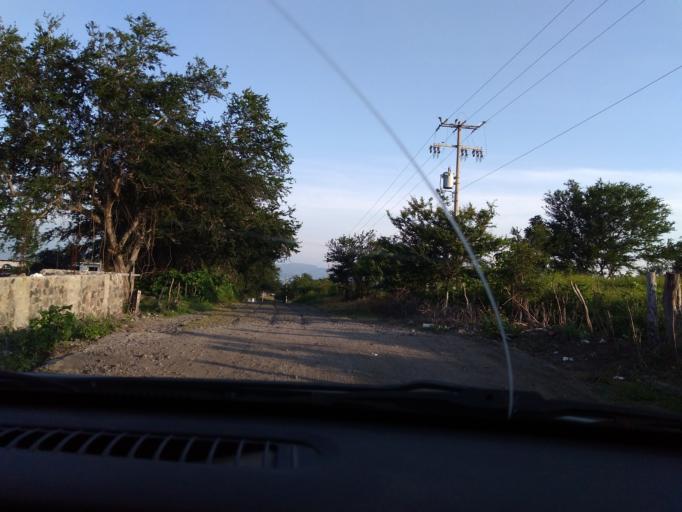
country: MX
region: Jalisco
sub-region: Tonila
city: San Marcos
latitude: 19.4494
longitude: -103.5113
